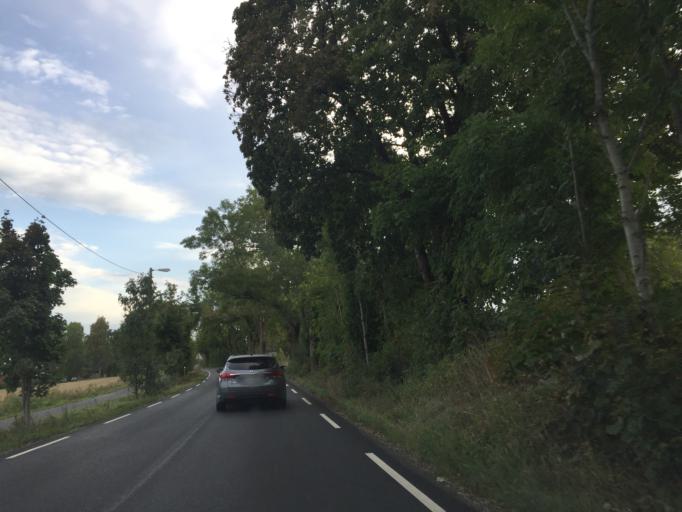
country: NO
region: Akershus
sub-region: As
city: As
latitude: 59.7078
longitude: 10.7715
